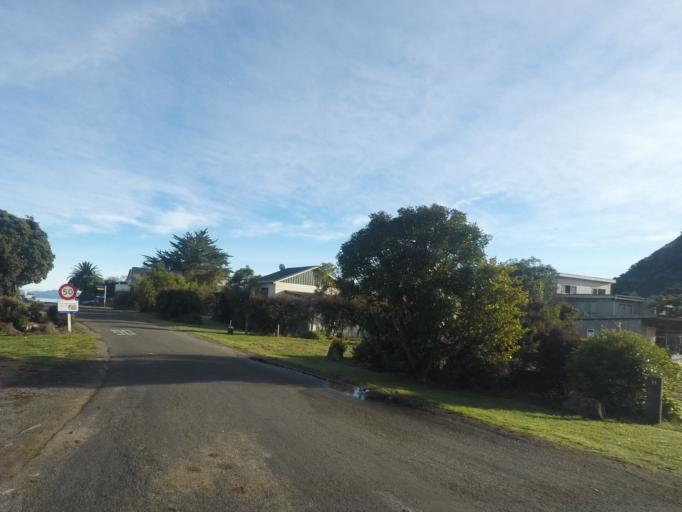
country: NZ
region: Tasman
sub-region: Tasman District
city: Takaka
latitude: -40.8121
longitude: 172.9162
